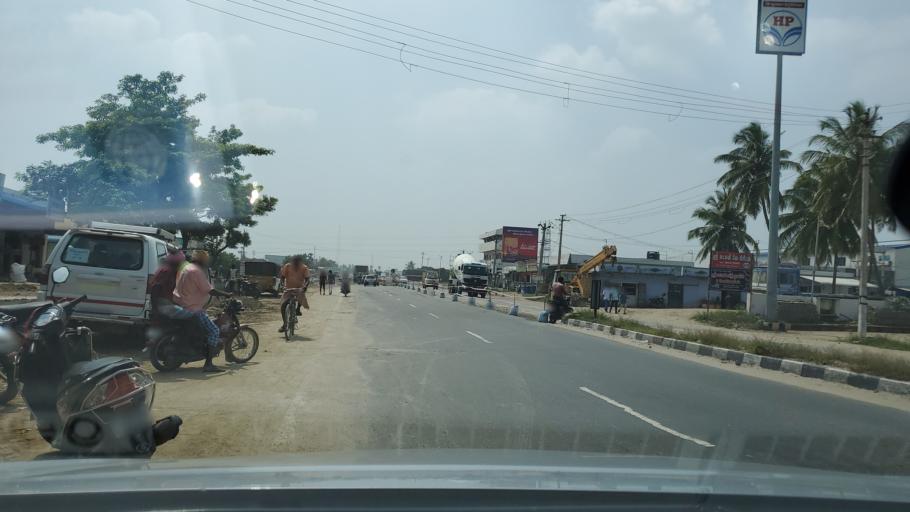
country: IN
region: Tamil Nadu
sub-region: Tiruppur
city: Kangayam
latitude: 10.9697
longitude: 77.4272
